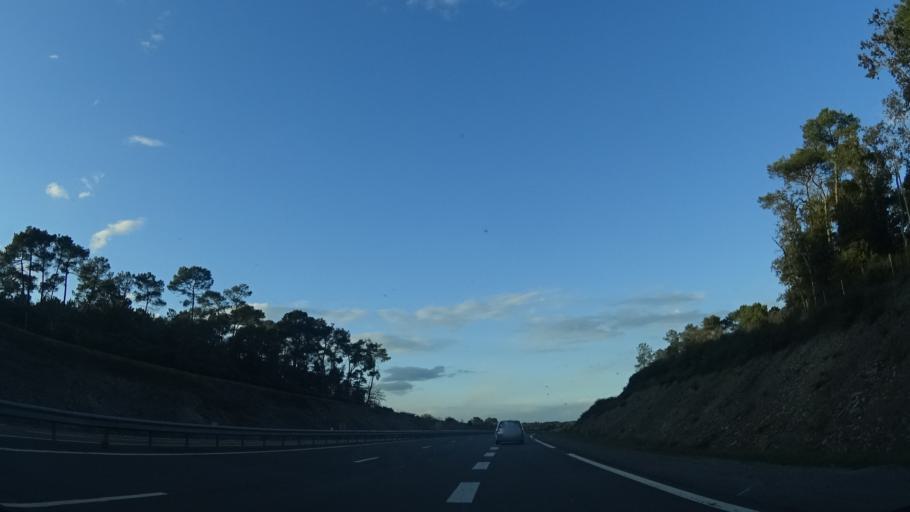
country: FR
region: Brittany
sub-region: Departement d'Ille-et-Vilaine
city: Bains-sur-Oust
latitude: 47.6793
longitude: -2.0650
